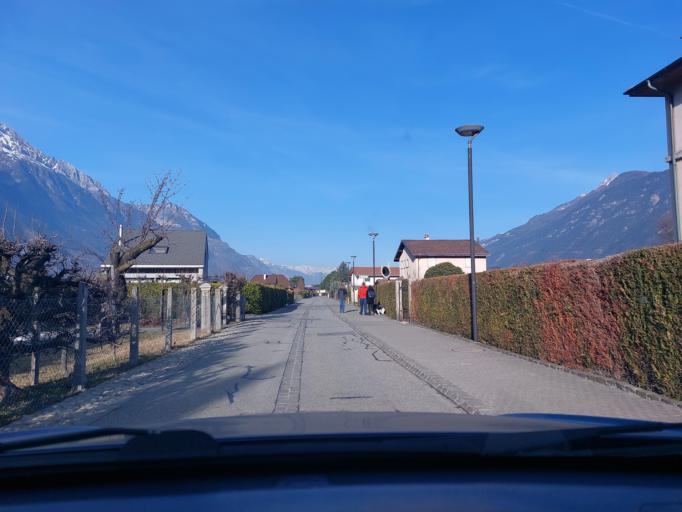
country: CH
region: Valais
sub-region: Martigny District
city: Martigny-Ville
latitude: 46.1071
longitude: 7.0789
